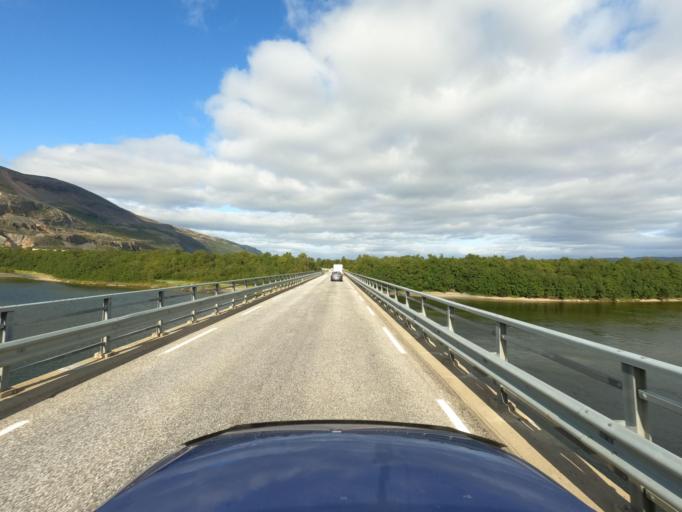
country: NO
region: Finnmark Fylke
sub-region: Porsanger
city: Lakselv
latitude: 70.0650
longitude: 24.9288
